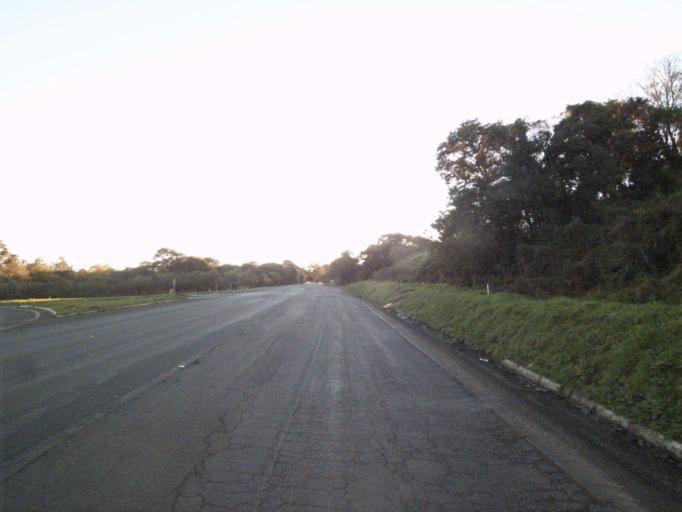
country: BR
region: Santa Catarina
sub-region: Sao Lourenco Do Oeste
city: Sao Lourenco dOeste
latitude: -26.8055
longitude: -53.1809
